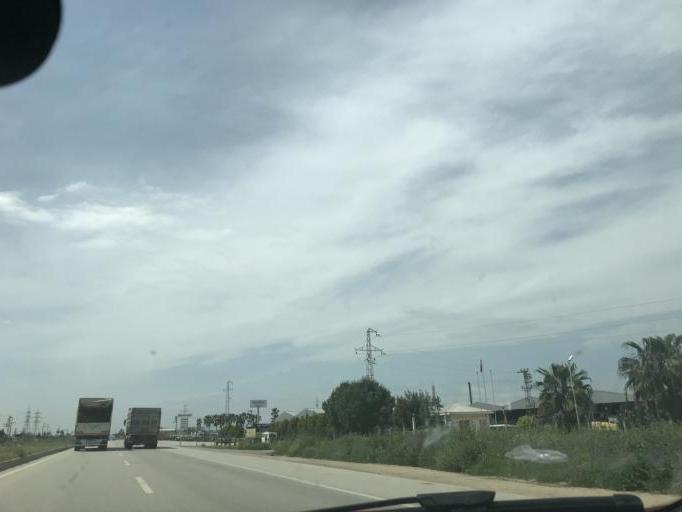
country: TR
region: Adana
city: Yuregir
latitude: 36.9786
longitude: 35.4629
